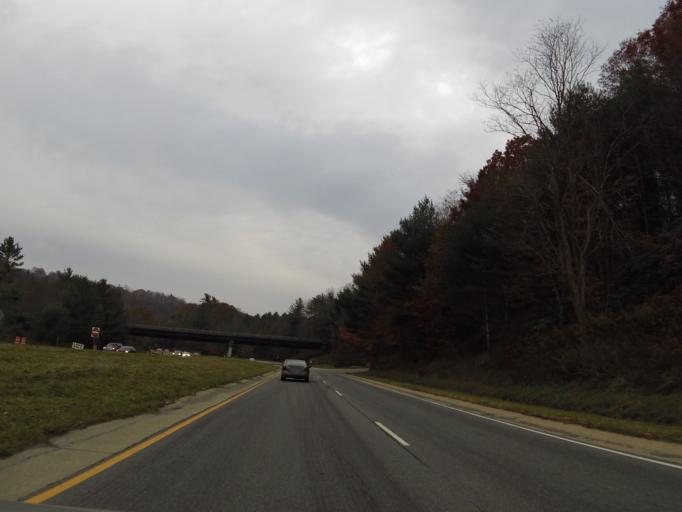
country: US
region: North Carolina
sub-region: Watauga County
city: Blowing Rock
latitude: 36.1490
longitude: -81.6614
